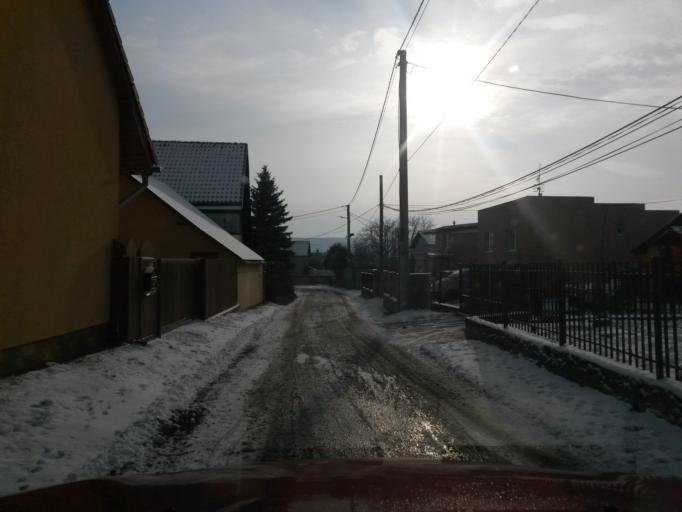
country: SK
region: Kosicky
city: Kosice
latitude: 48.8067
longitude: 21.2458
